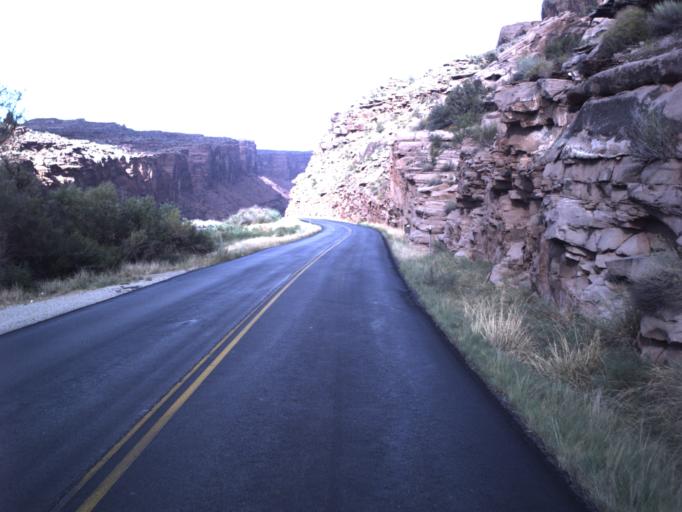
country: US
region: Utah
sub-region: Grand County
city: Moab
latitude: 38.6143
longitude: -109.5297
